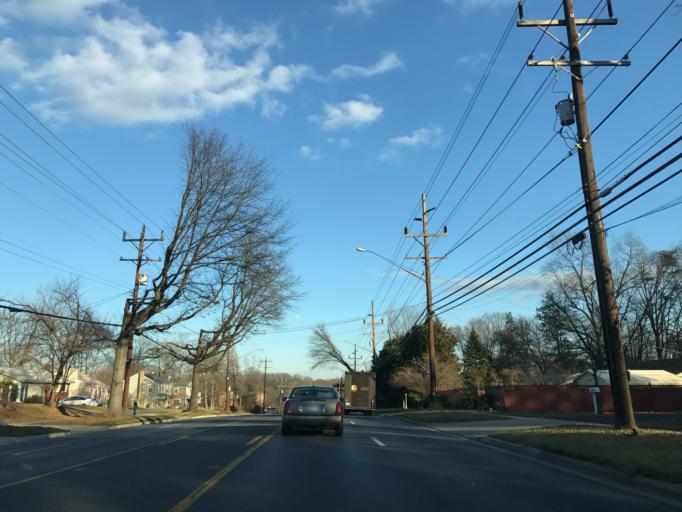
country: US
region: Maryland
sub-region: Montgomery County
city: North Bethesda
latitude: 39.0538
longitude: -77.0981
